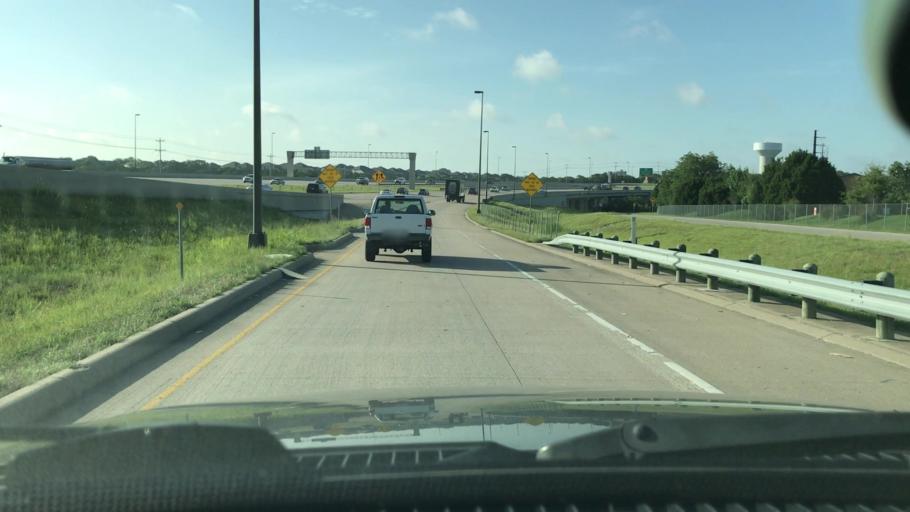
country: US
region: Texas
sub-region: Williamson County
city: Cedar Park
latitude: 30.4992
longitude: -97.8054
